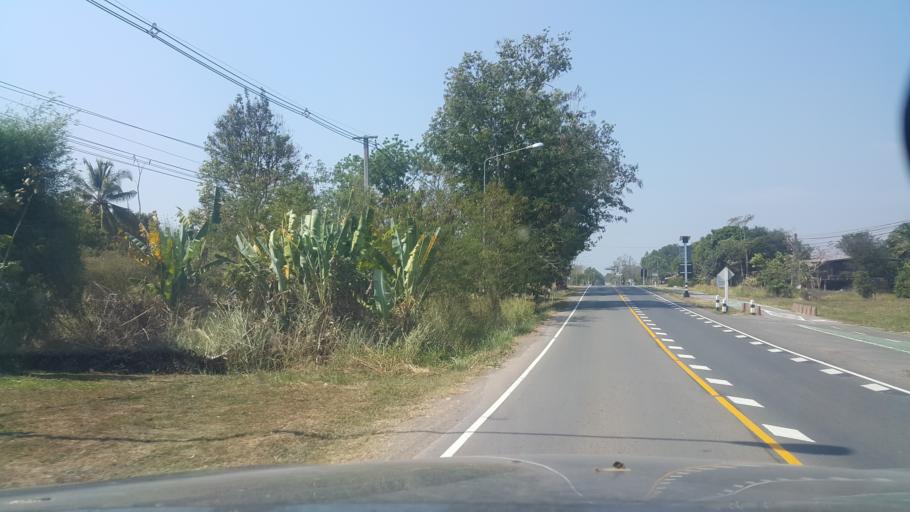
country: TH
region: Nakhon Ratchasima
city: Wang Nam Khiao
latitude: 14.3619
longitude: 101.9154
